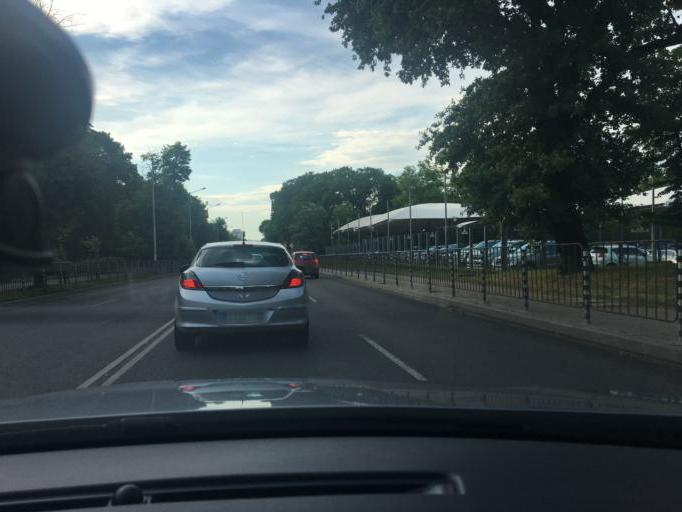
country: BG
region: Sofia-Capital
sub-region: Stolichna Obshtina
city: Sofia
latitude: 42.6833
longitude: 23.3347
